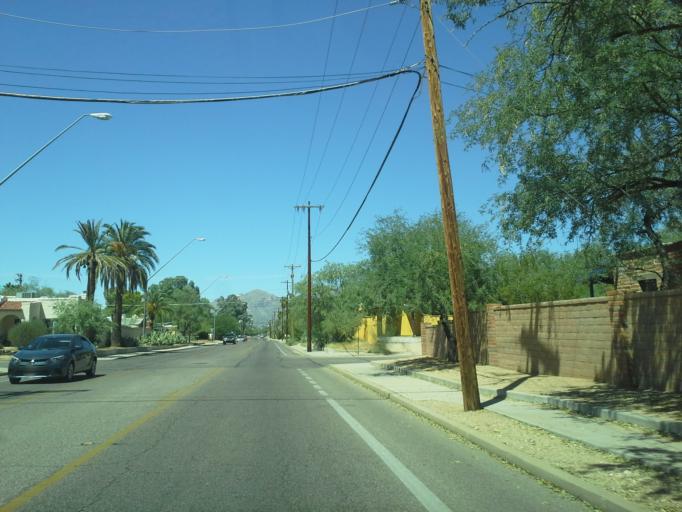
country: US
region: Arizona
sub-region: Pima County
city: Tucson
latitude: 32.2382
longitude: -110.9353
